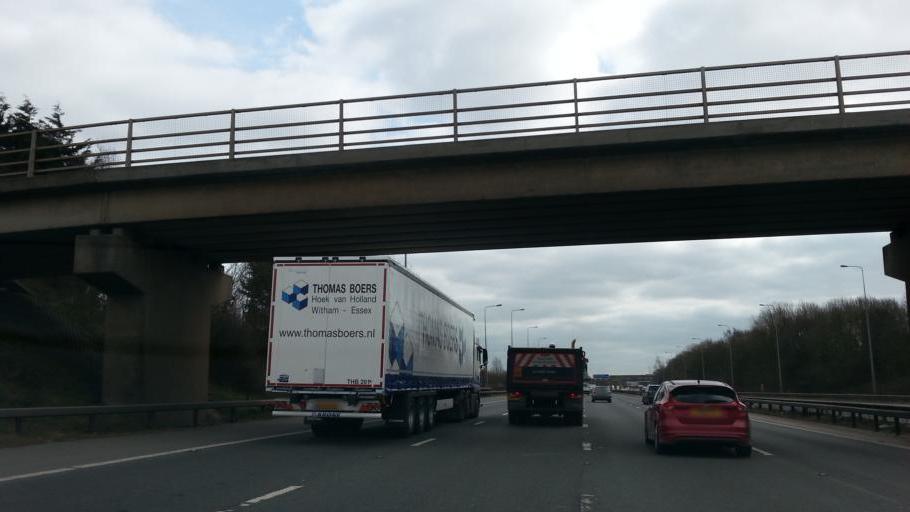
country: GB
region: England
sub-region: Warrington
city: Croft
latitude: 53.4051
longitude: -2.5187
